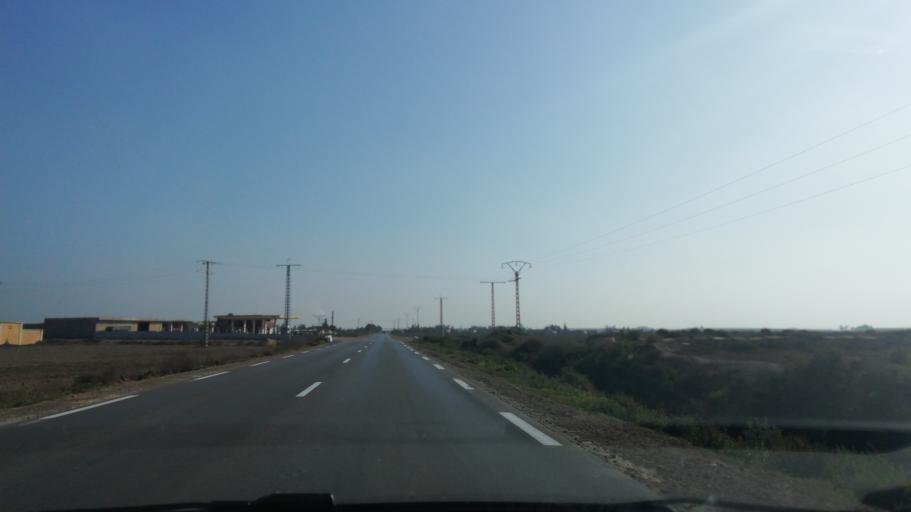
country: DZ
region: Mostaganem
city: Mostaganem
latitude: 35.7491
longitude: 0.0298
